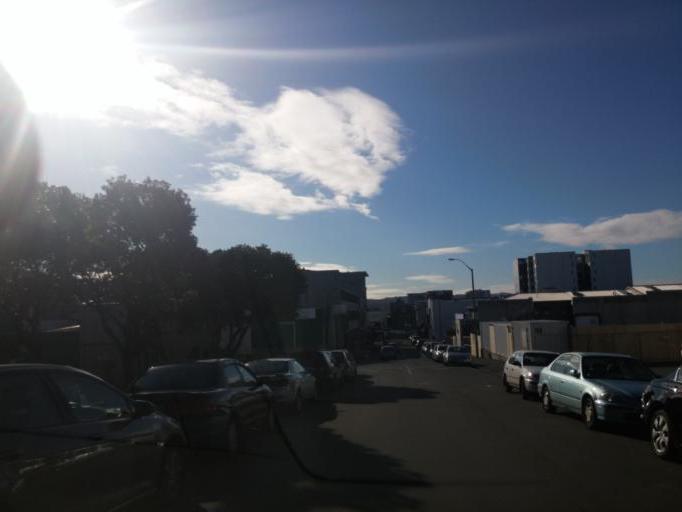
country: NZ
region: Wellington
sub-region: Wellington City
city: Wellington
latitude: -41.3000
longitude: 174.7733
